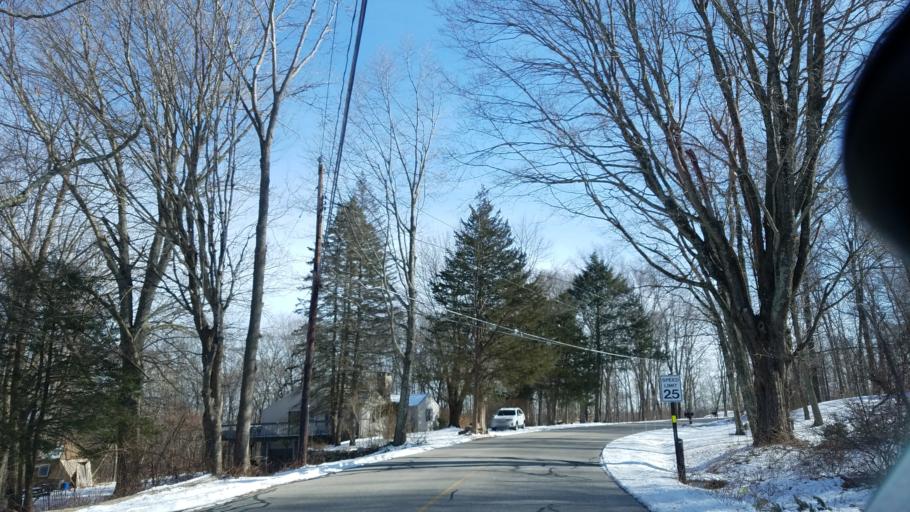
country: US
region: Connecticut
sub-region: Tolland County
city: Coventry Lake
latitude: 41.7279
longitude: -72.3650
